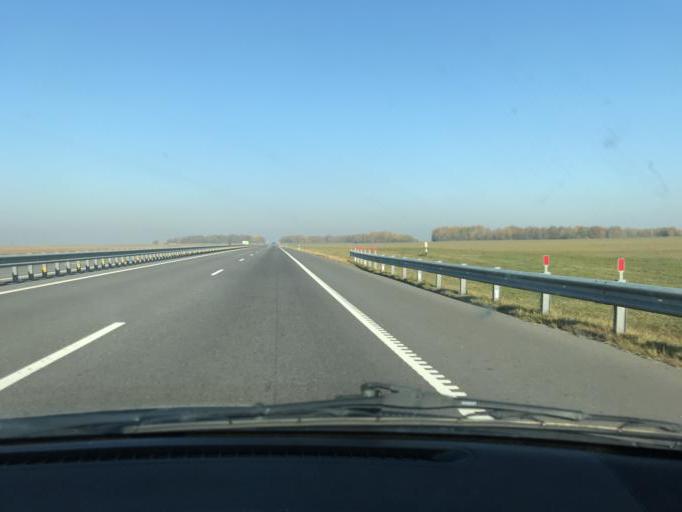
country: BY
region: Minsk
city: Slutsk
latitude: 53.1847
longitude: 27.5513
